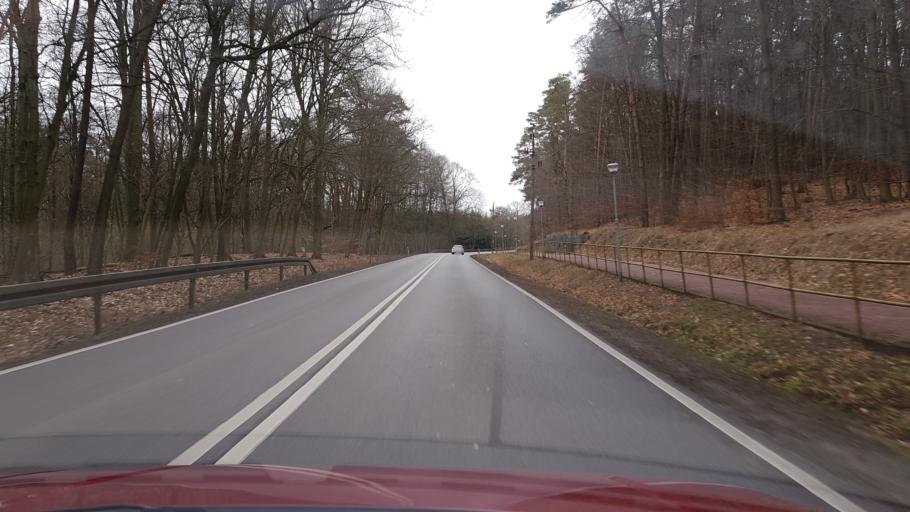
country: PL
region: West Pomeranian Voivodeship
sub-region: Szczecin
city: Szczecin
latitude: 53.4869
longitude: 14.4835
